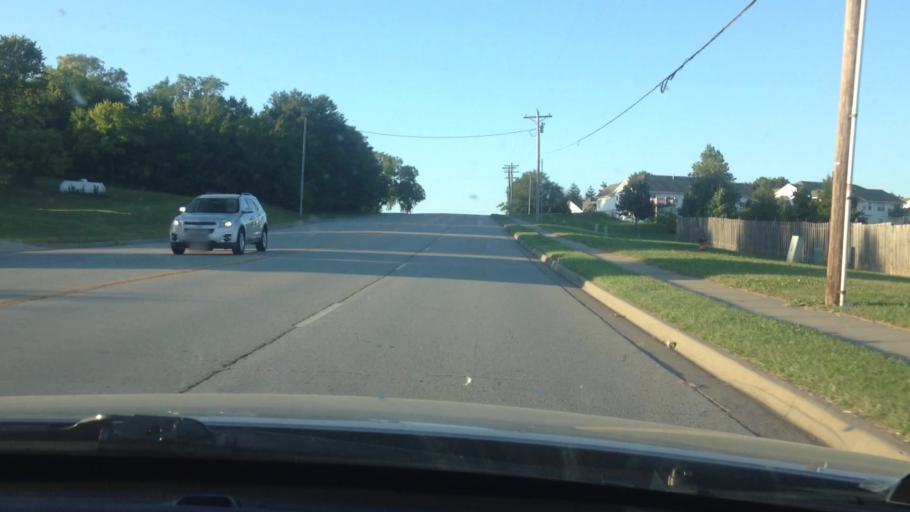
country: US
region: Missouri
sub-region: Platte County
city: Platte City
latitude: 39.3414
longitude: -94.7611
